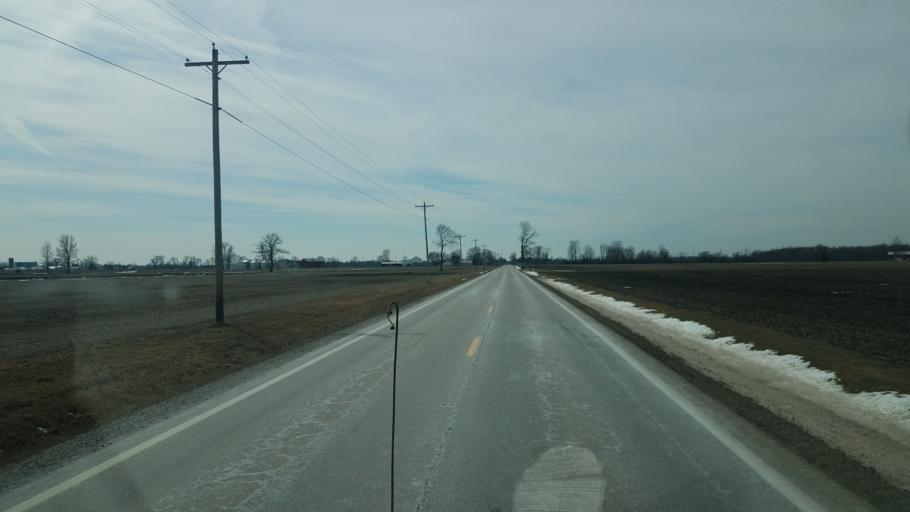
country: US
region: Ohio
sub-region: Delaware County
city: Delaware
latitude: 40.3123
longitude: -83.0035
